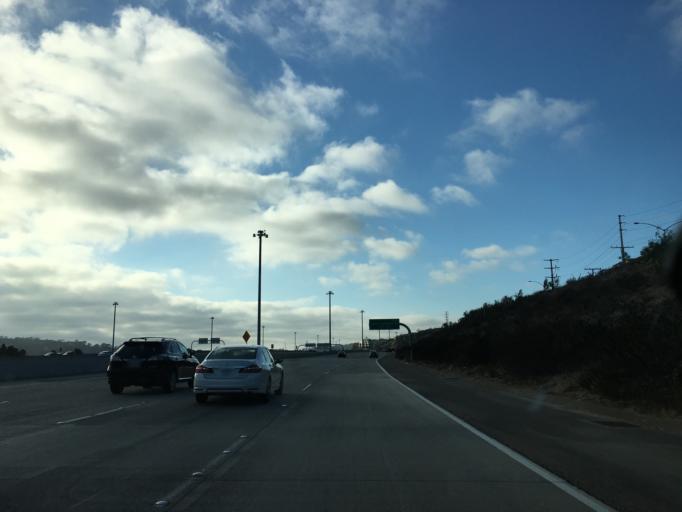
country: US
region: California
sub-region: San Diego County
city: Del Mar
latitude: 32.9086
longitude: -117.2257
